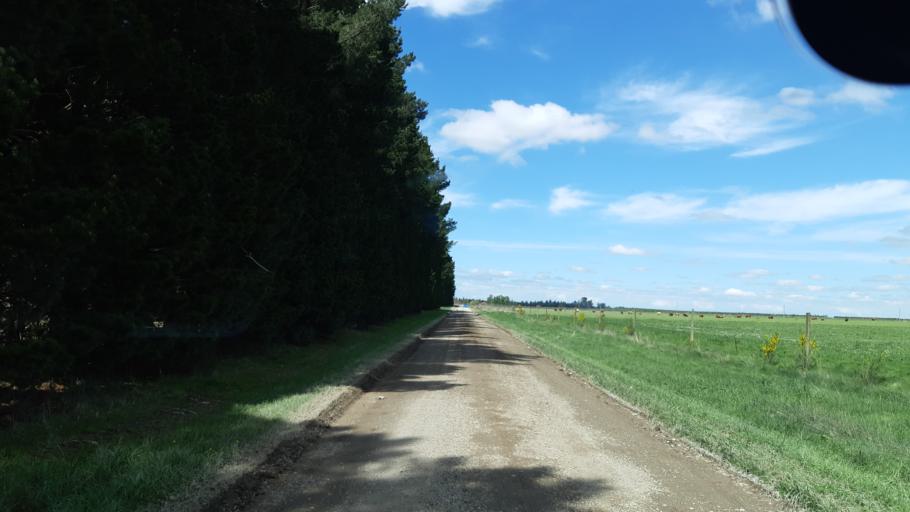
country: NZ
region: Canterbury
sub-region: Ashburton District
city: Methven
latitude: -43.6907
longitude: 171.4518
